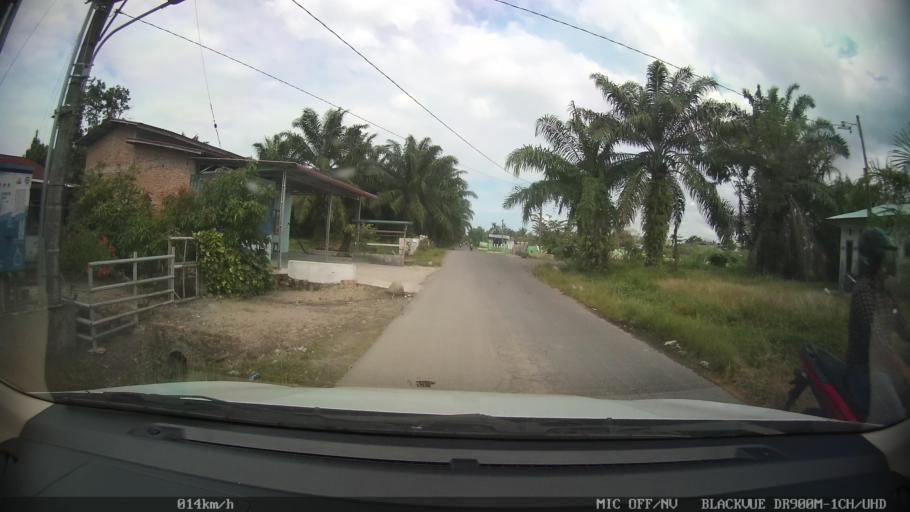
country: ID
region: North Sumatra
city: Sunggal
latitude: 3.6357
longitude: 98.6000
